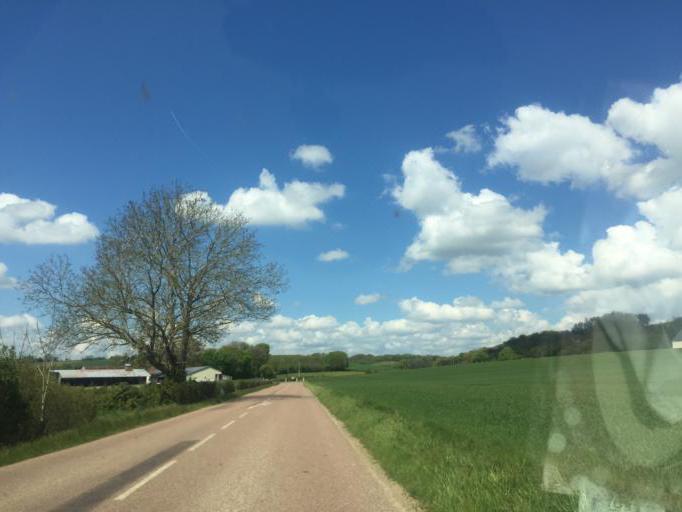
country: FR
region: Bourgogne
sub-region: Departement de l'Yonne
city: Fontenailles
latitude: 47.4791
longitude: 3.4279
